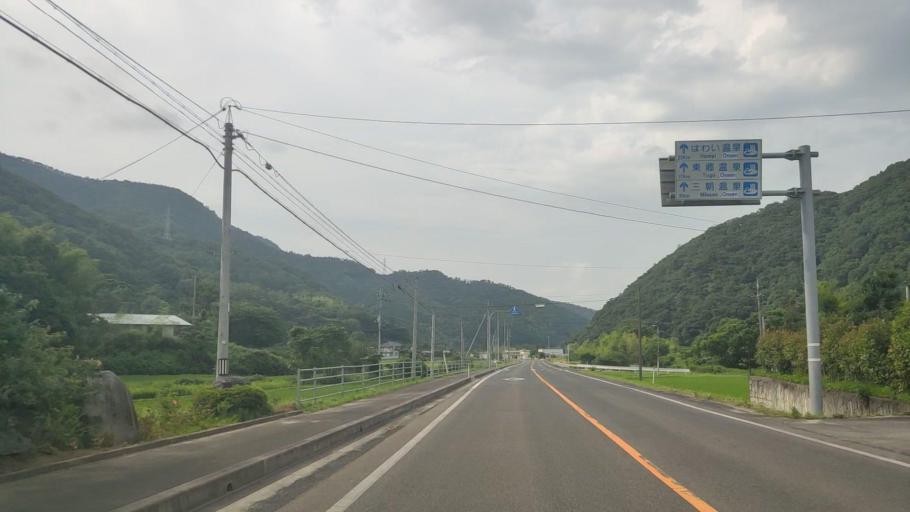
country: JP
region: Tottori
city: Kurayoshi
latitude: 35.3698
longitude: 133.8500
